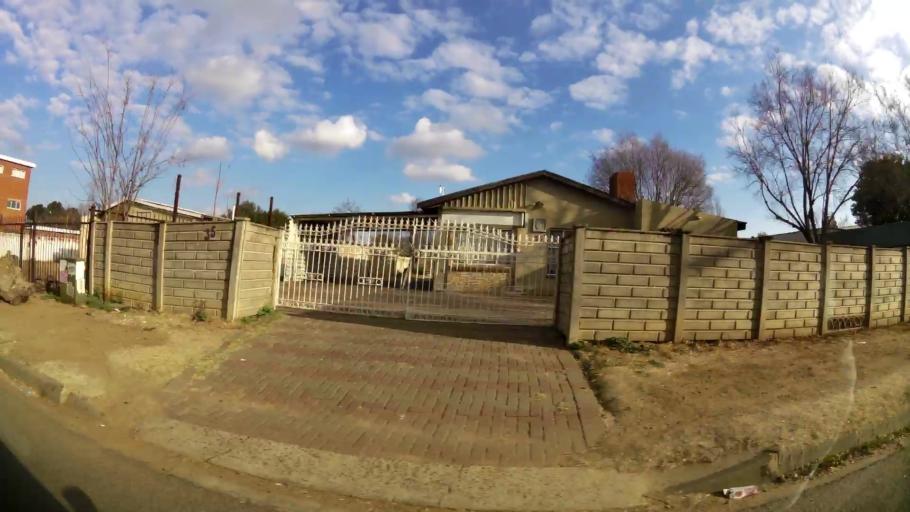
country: ZA
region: Orange Free State
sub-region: Mangaung Metropolitan Municipality
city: Bloemfontein
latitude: -29.1022
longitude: 26.1928
